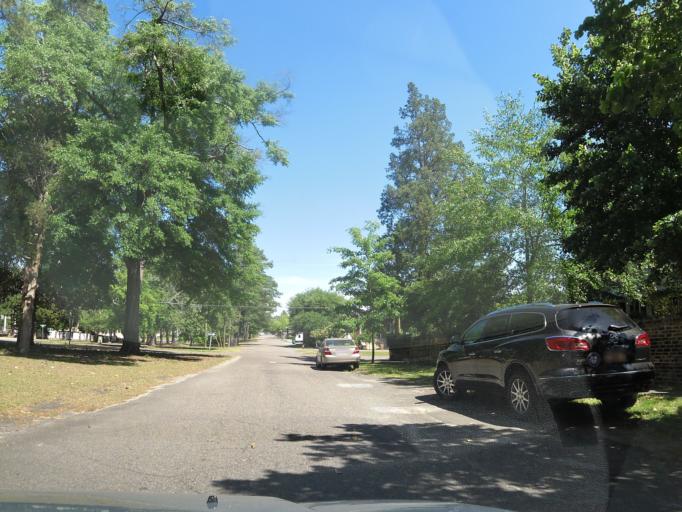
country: US
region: South Carolina
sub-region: Aiken County
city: Aiken
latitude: 33.5646
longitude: -81.7250
